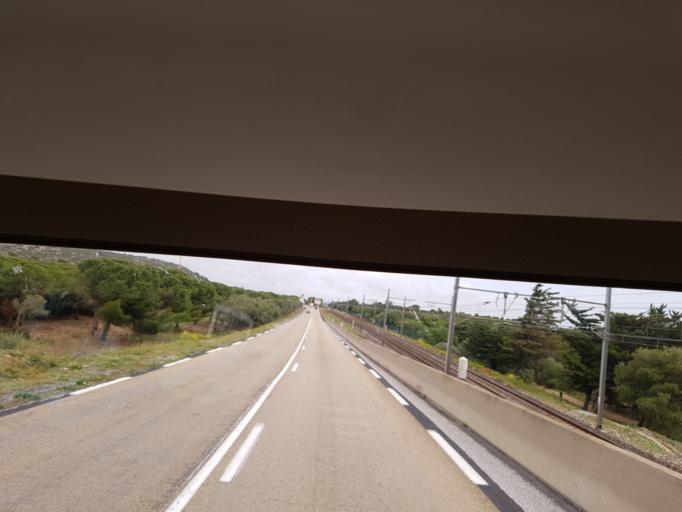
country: FR
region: Languedoc-Roussillon
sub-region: Departement de l'Aude
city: Leucate
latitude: 42.8741
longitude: 2.9922
